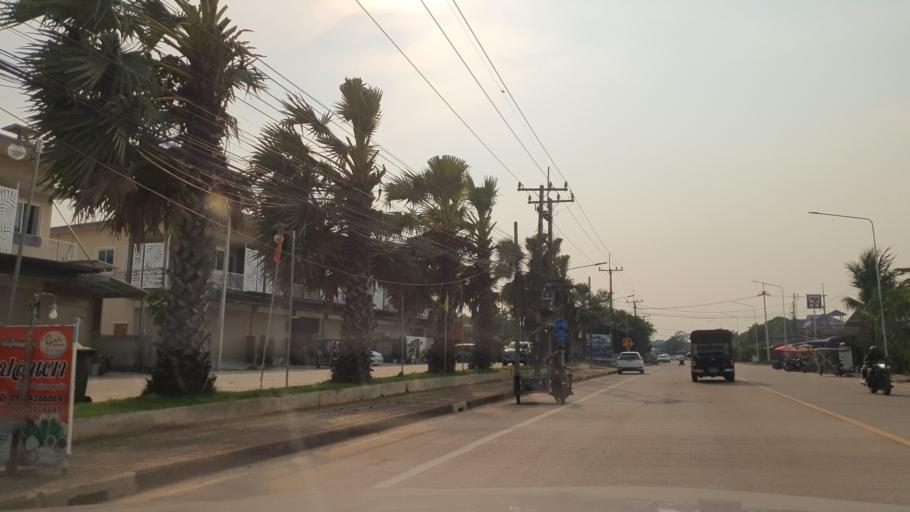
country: TH
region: Rayong
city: Rayong
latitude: 12.6192
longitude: 101.4065
